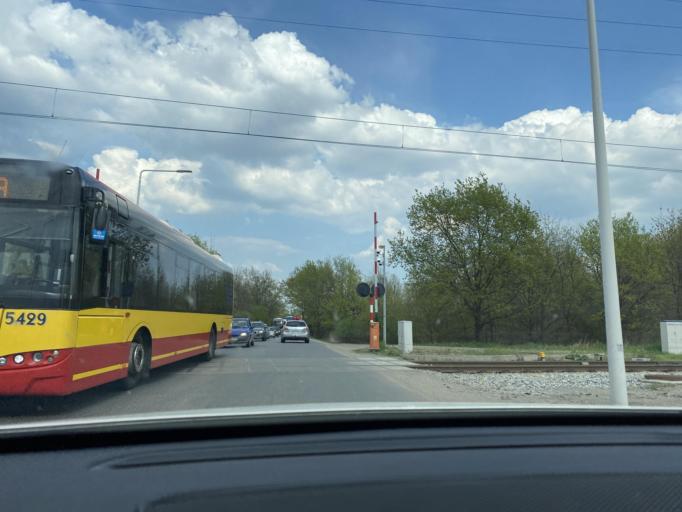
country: PL
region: Lower Silesian Voivodeship
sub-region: Powiat wroclawski
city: Wilczyce
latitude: 51.1205
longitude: 17.1164
